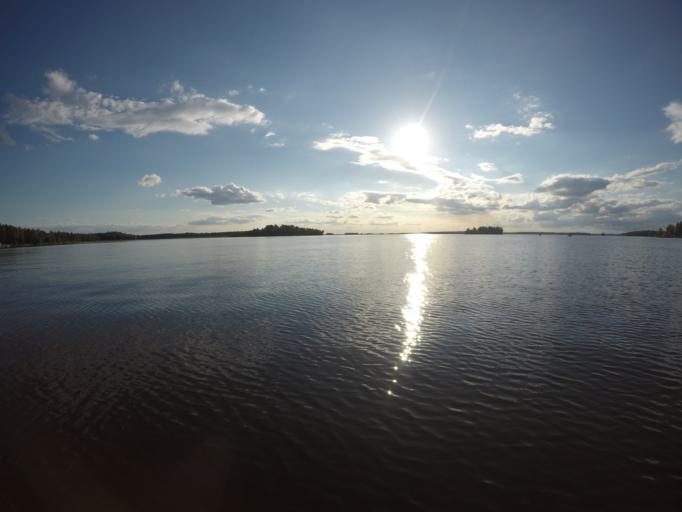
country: SE
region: Soedermanland
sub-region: Eskilstuna Kommun
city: Kvicksund
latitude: 59.4515
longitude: 16.3036
